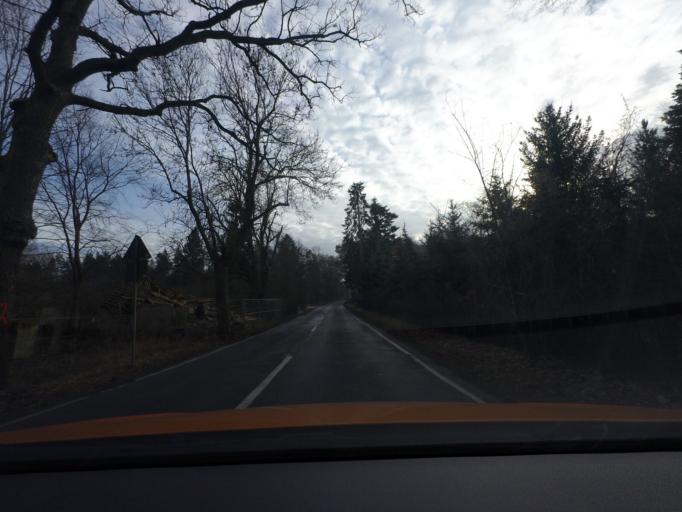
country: DE
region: Brandenburg
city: Wandlitz
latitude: 52.7318
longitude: 13.3681
